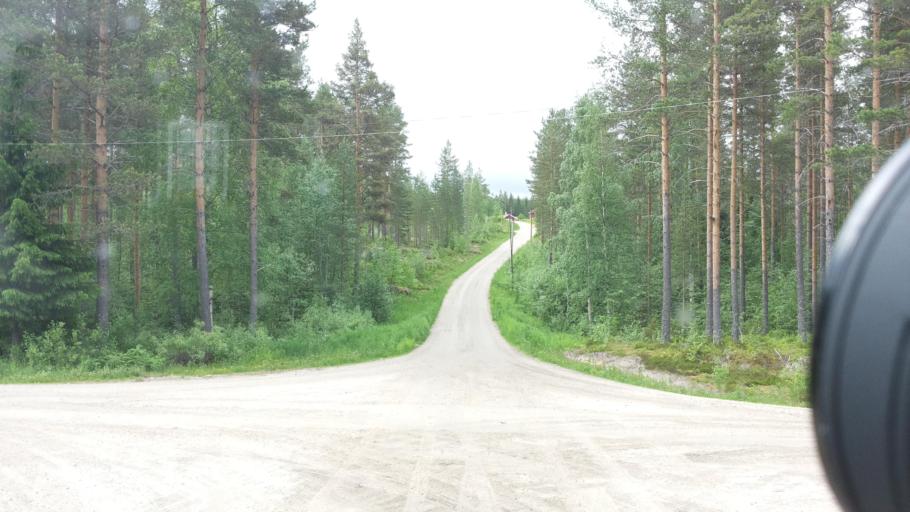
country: SE
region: Gaevleborg
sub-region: Ovanakers Kommun
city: Edsbyn
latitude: 61.5018
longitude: 15.3379
